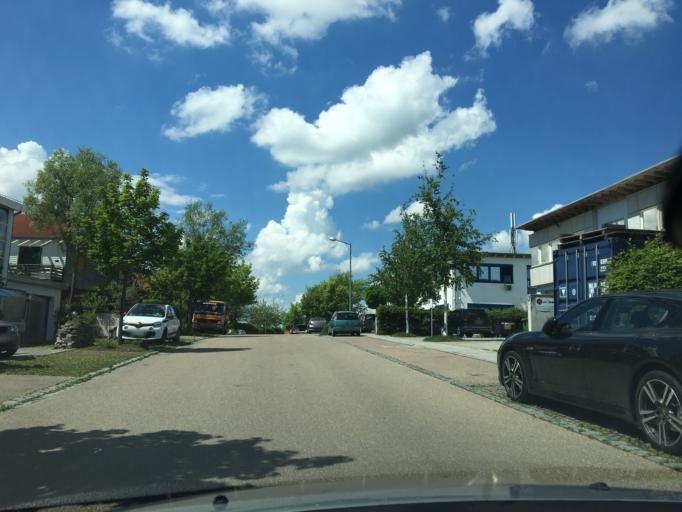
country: DE
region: Bavaria
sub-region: Upper Bavaria
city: Haimhausen
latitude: 48.3185
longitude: 11.5606
